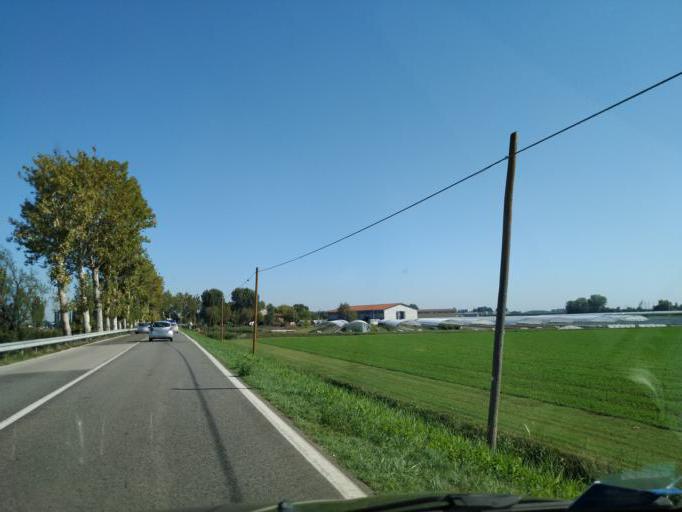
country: IT
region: Emilia-Romagna
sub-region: Provincia di Bologna
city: Decima
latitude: 44.6899
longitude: 11.2206
